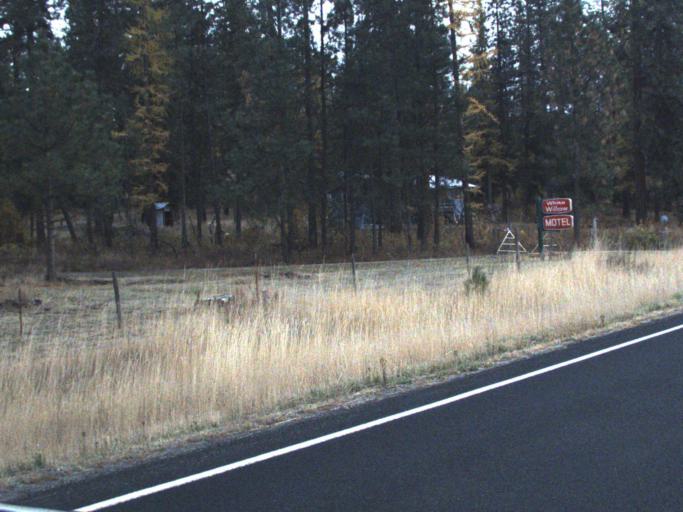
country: US
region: Washington
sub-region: Lincoln County
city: Davenport
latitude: 47.9700
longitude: -118.3020
